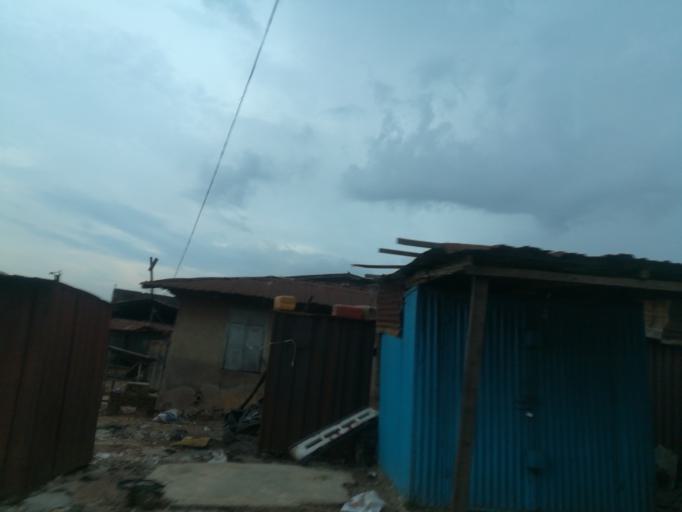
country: NG
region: Oyo
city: Moniya
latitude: 7.4656
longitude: 3.9111
